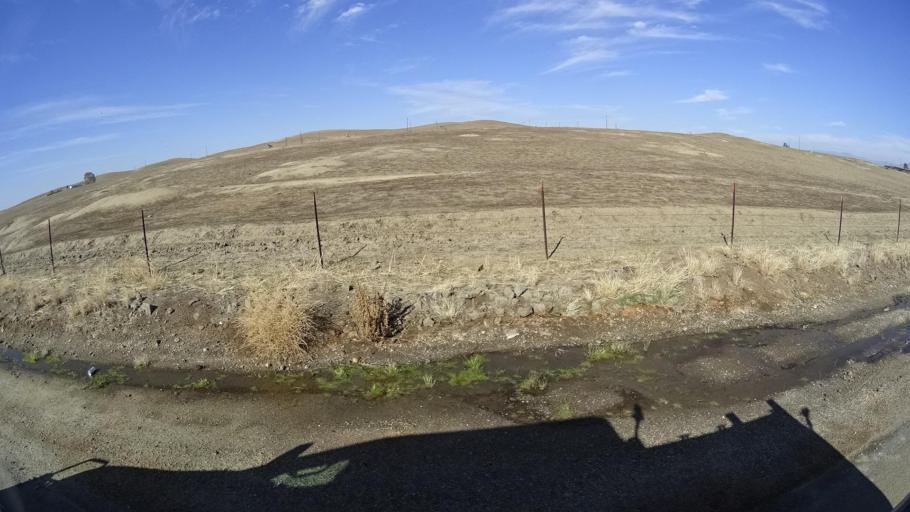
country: US
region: California
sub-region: Tulare County
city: Richgrove
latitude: 35.6324
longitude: -118.9616
